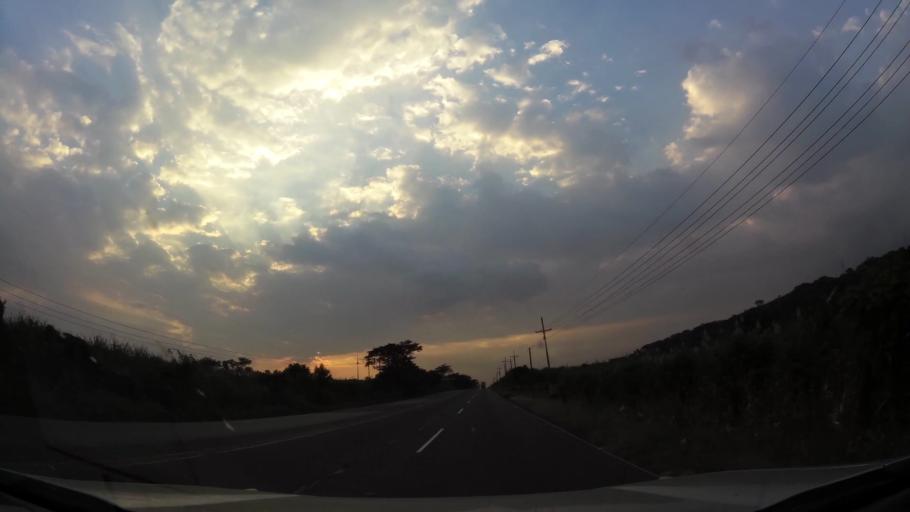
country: GT
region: Escuintla
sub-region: Municipio de Masagua
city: Masagua
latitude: 14.2676
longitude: -90.8774
